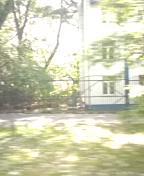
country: RU
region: Moscow
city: Pokrovskoye-Streshnevo
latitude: 55.8181
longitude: 37.4683
